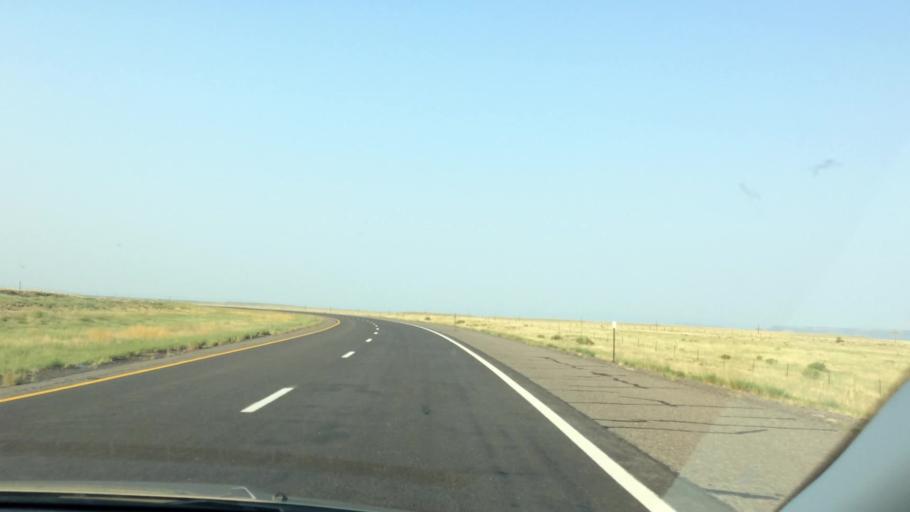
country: US
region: New Mexico
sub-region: Colfax County
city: Raton
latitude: 36.7212
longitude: -104.4718
